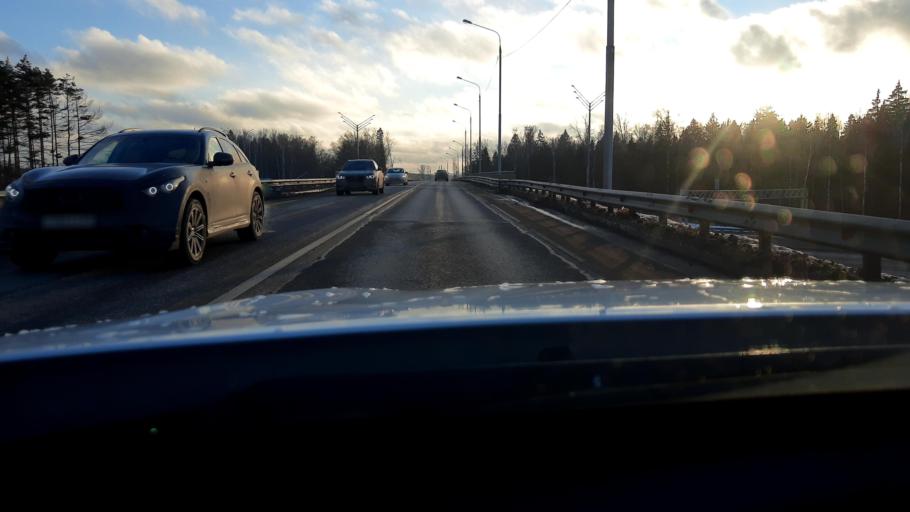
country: RU
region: Moscow
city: Khimki
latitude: 55.9460
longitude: 37.4452
